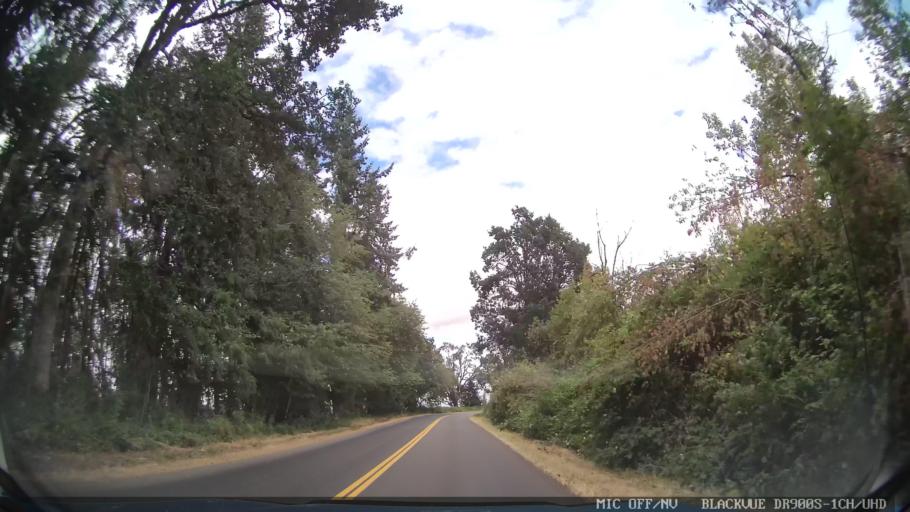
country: US
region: Oregon
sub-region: Marion County
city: Aumsville
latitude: 44.8646
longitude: -122.8487
